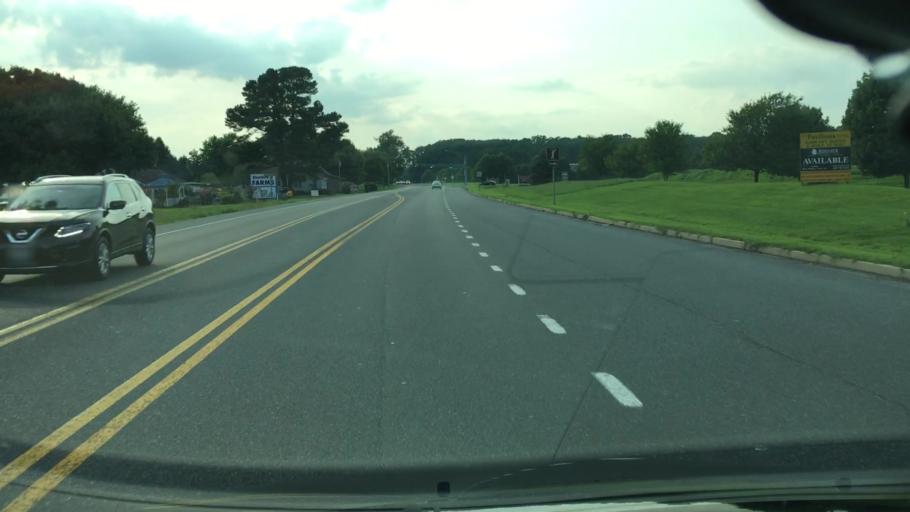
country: US
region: Maryland
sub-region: Worcester County
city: Ocean Pines
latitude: 38.3860
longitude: -75.1836
